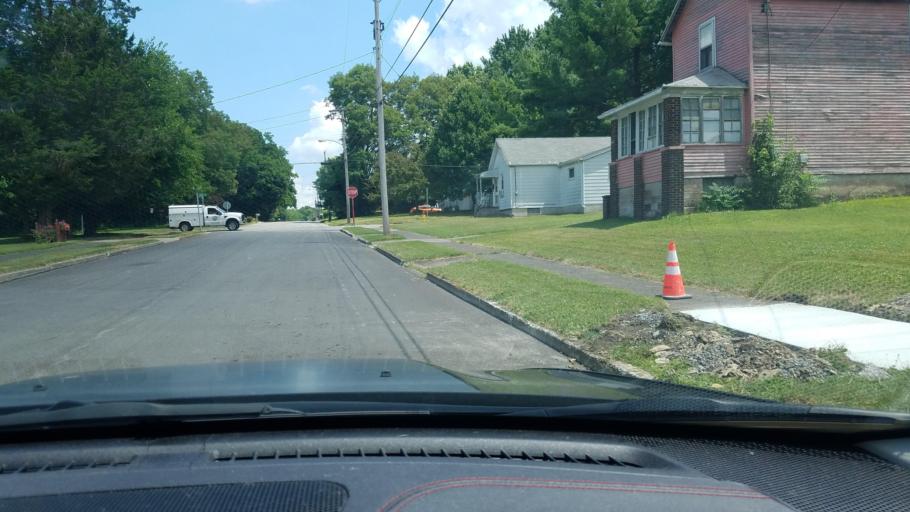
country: US
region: Ohio
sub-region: Mahoning County
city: Campbell
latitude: 41.0775
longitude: -80.5843
